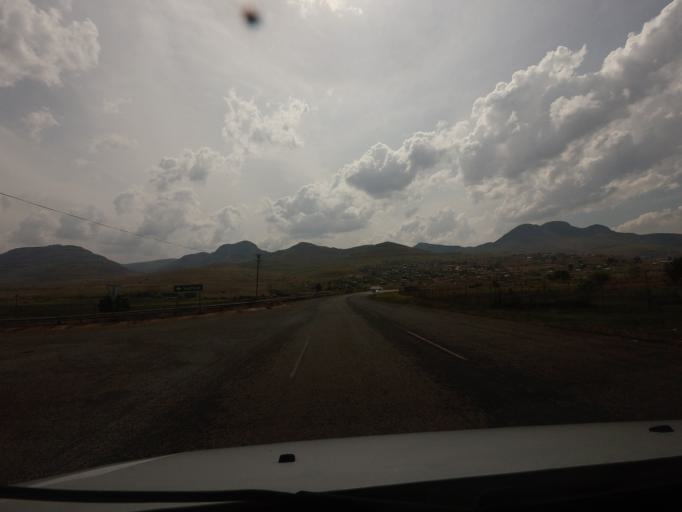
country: ZA
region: Mpumalanga
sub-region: Ehlanzeni District
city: Graksop
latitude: -24.6812
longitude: 30.8071
